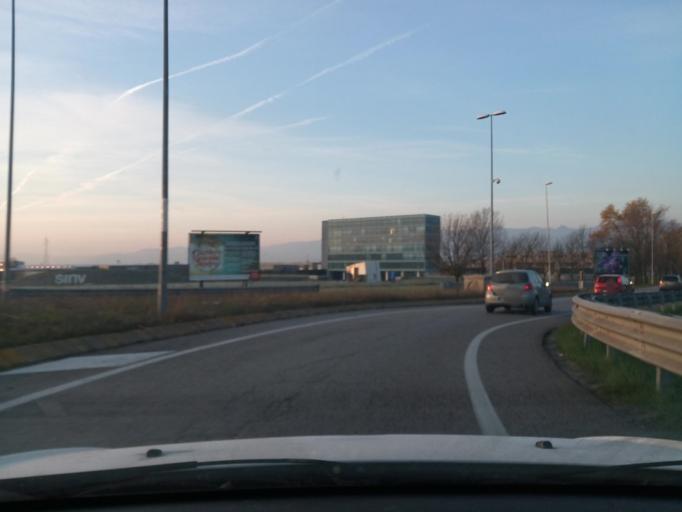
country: IT
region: Veneto
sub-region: Provincia di Vicenza
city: Zane
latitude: 45.7252
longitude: 11.4208
